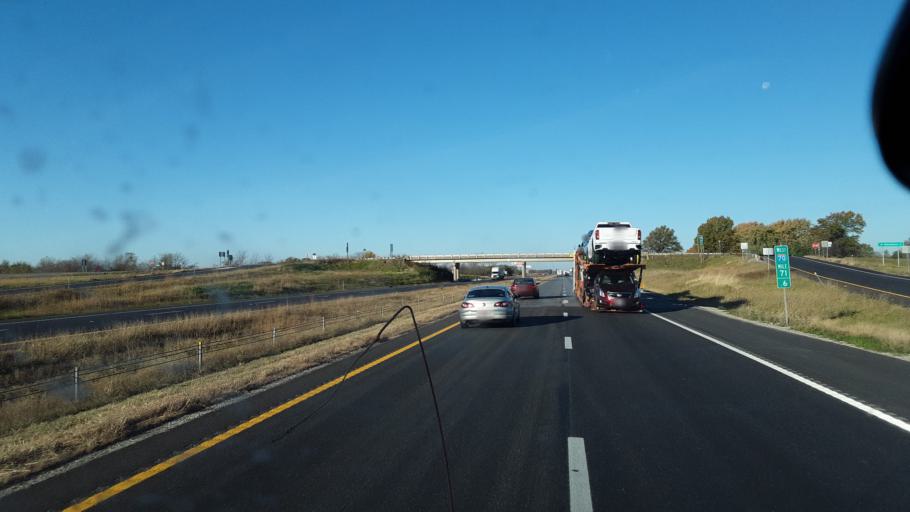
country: US
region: Missouri
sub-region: Saline County
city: Sweet Springs
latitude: 38.9736
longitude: -93.3292
